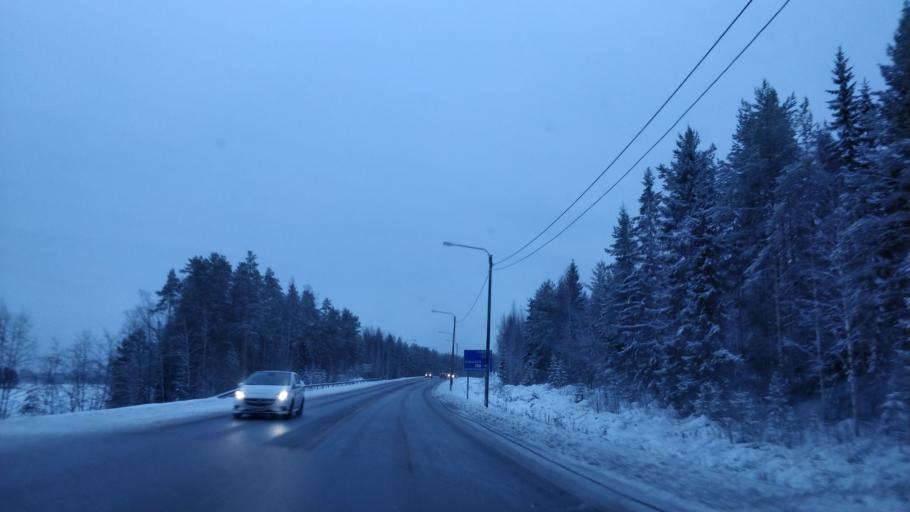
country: FI
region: Central Finland
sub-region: AEaenekoski
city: AEaenekoski
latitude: 62.8075
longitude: 25.8074
